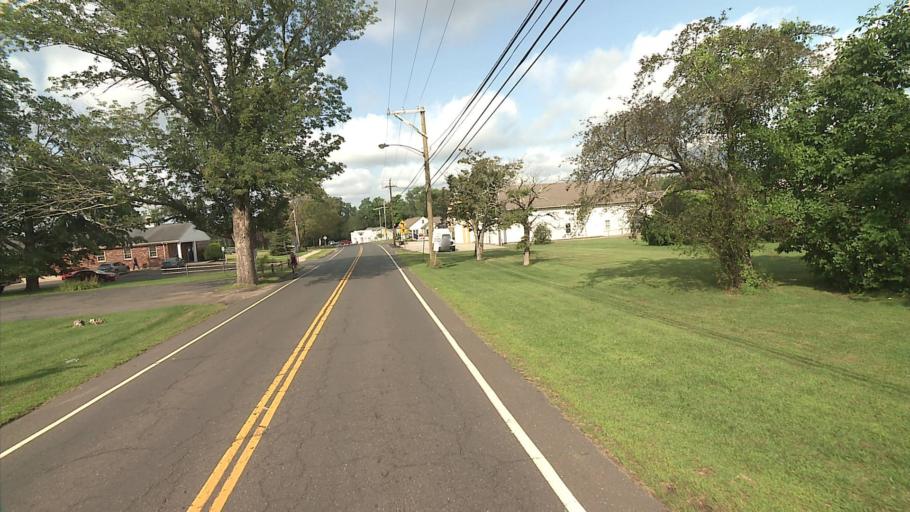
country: US
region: Connecticut
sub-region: Middlesex County
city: Moodus
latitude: 41.5058
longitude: -72.4455
